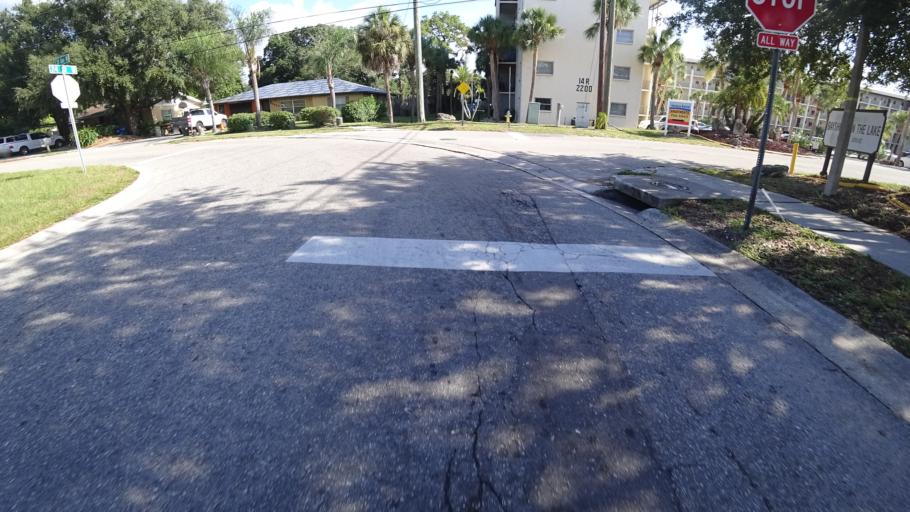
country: US
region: Florida
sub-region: Manatee County
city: South Bradenton
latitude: 27.4672
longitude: -82.5855
